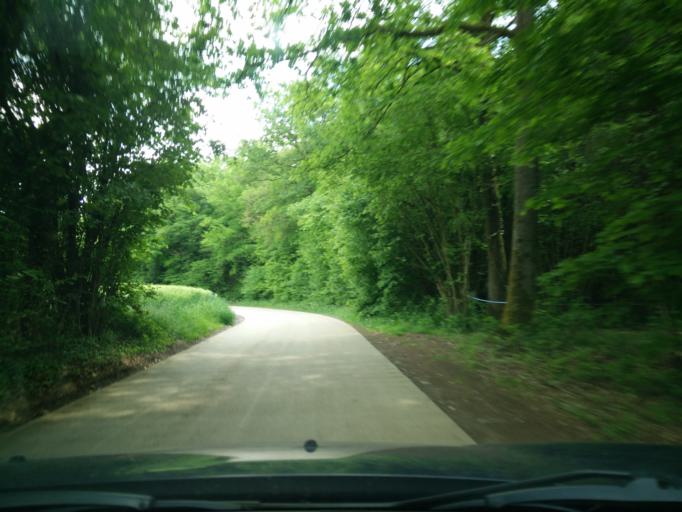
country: FR
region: Champagne-Ardenne
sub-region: Departement des Ardennes
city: Vireux-Molhain
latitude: 50.0888
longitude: 4.6073
